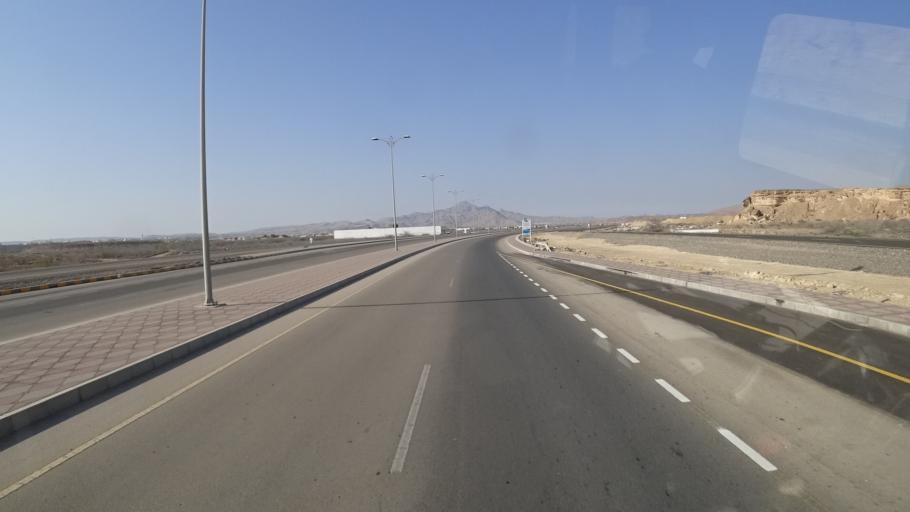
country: OM
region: Ash Sharqiyah
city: Sur
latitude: 22.5911
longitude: 59.4778
